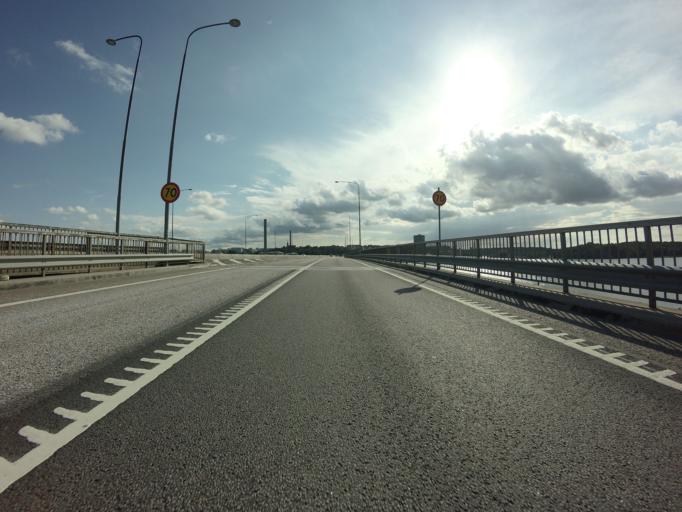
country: SE
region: Stockholm
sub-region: Lidingo
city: Lidingoe
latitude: 59.3624
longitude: 18.1136
